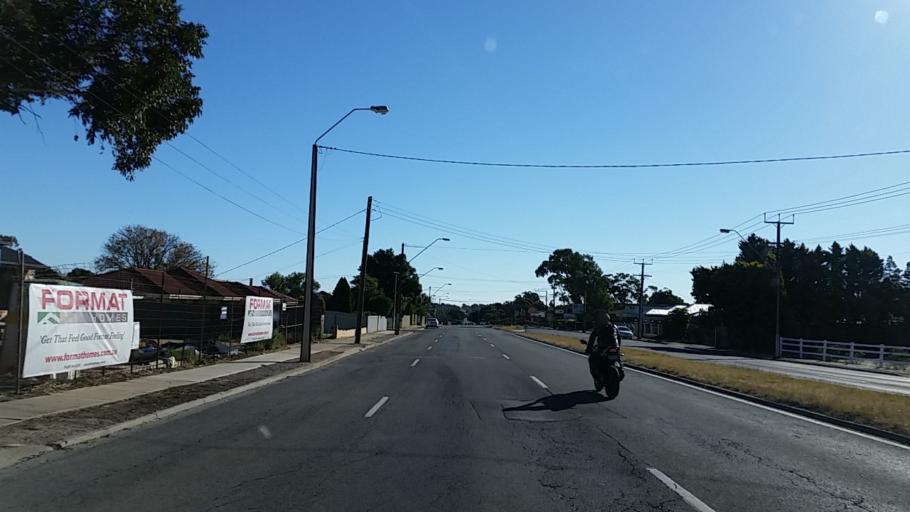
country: AU
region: South Australia
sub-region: Tea Tree Gully
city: Hope Valley
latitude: -34.8276
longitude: 138.6975
